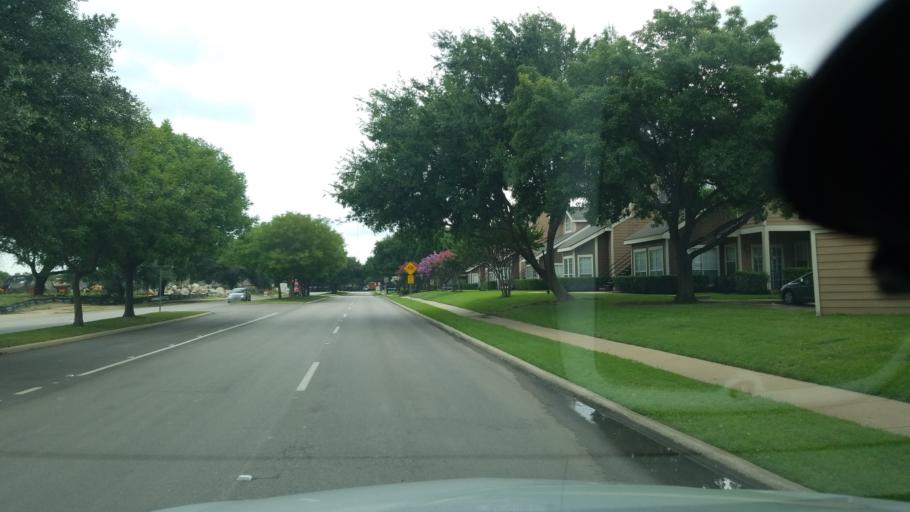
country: US
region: Texas
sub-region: Dallas County
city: Farmers Branch
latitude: 32.9384
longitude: -96.9469
